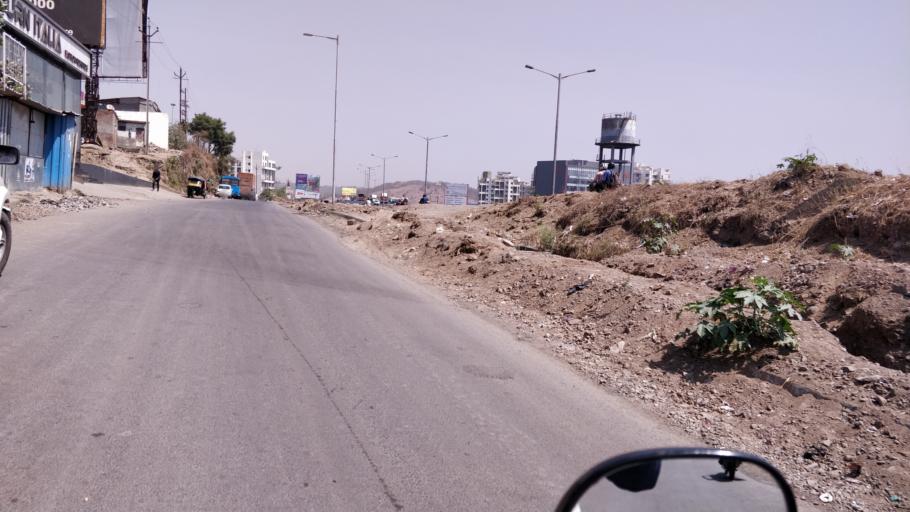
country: IN
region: Maharashtra
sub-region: Pune Division
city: Kharakvasla
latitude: 18.5165
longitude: 73.7687
